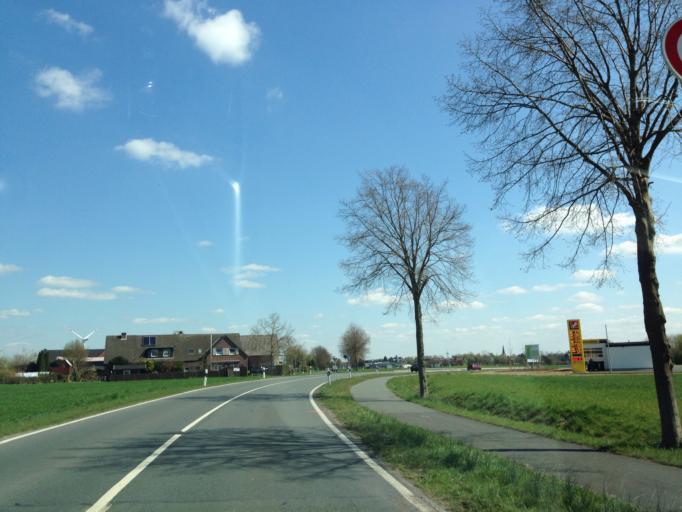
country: DE
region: North Rhine-Westphalia
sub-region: Regierungsbezirk Munster
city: Muenster
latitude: 51.8935
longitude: 7.5829
